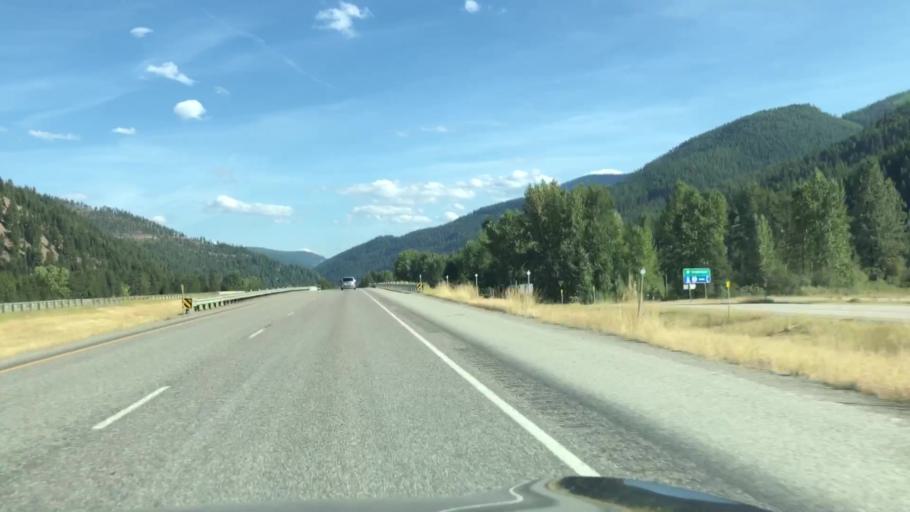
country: US
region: Montana
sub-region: Sanders County
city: Thompson Falls
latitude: 47.3769
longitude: -115.3517
